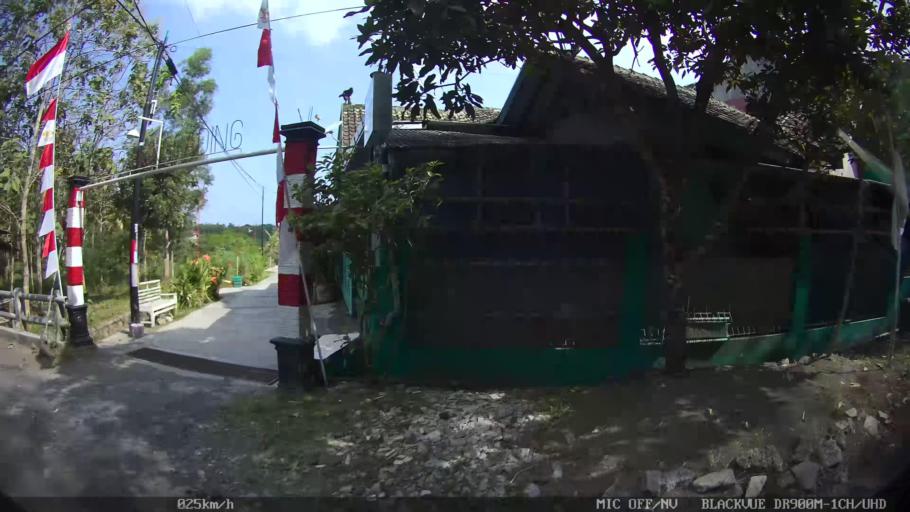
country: ID
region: Daerah Istimewa Yogyakarta
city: Bantul
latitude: -7.8594
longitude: 110.3034
